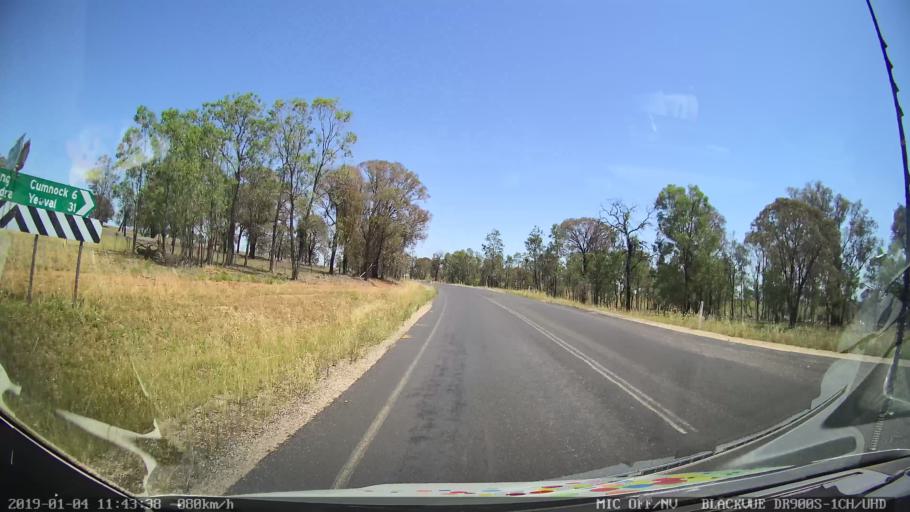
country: AU
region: New South Wales
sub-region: Cabonne
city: Molong
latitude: -32.9668
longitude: 148.7830
